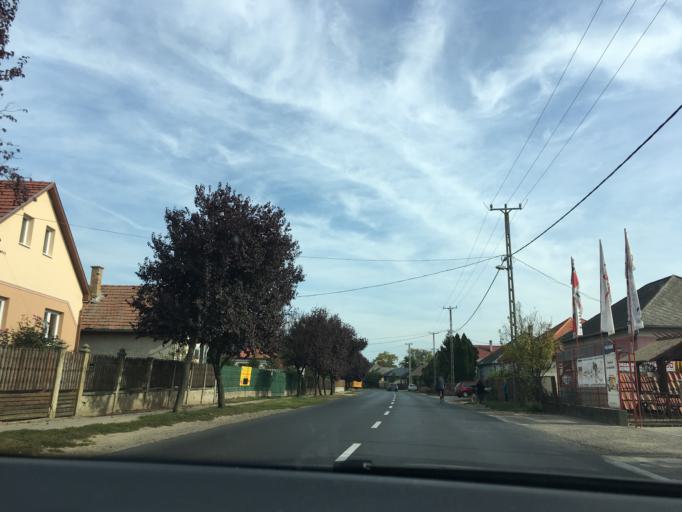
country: HU
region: Szabolcs-Szatmar-Bereg
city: Kallosemjen
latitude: 47.8591
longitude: 21.9176
